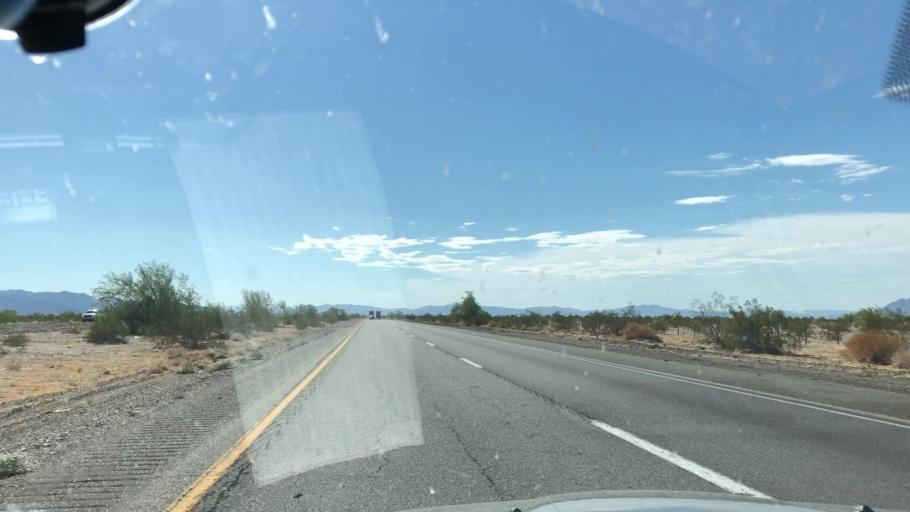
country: US
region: California
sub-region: Riverside County
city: Mesa Verde
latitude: 33.6537
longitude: -115.1459
